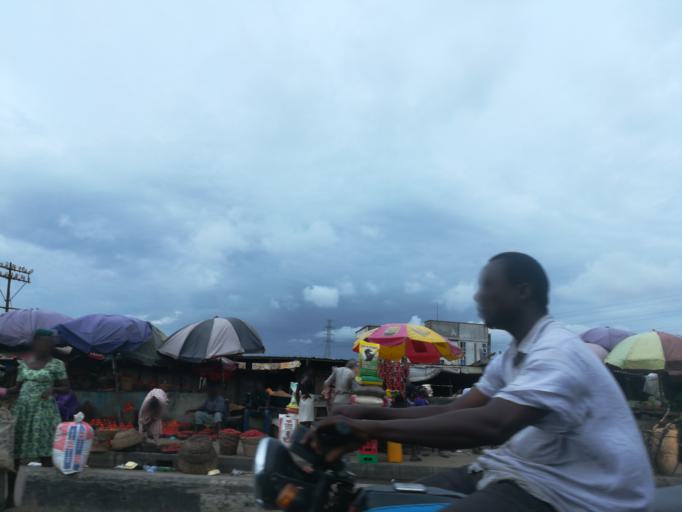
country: NG
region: Lagos
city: Ebute Metta
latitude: 6.4707
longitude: 3.3829
